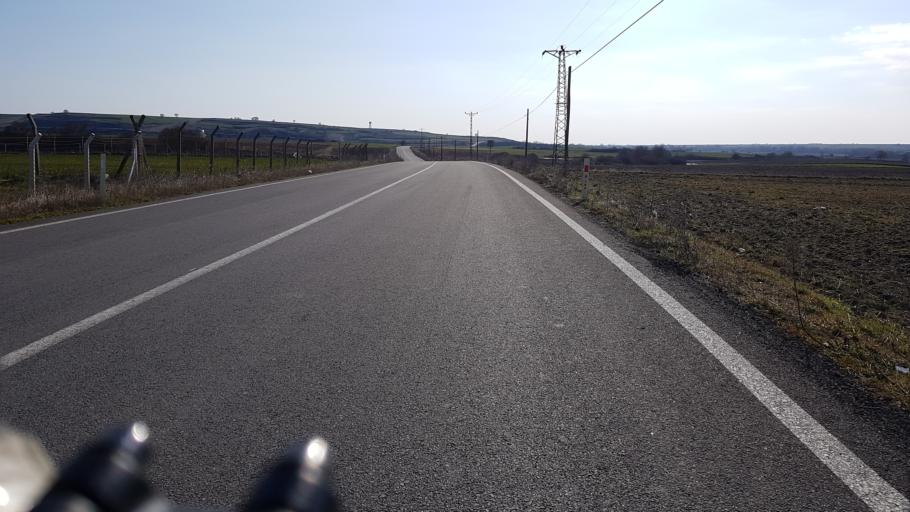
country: TR
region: Tekirdag
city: Saray
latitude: 41.3663
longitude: 27.8590
